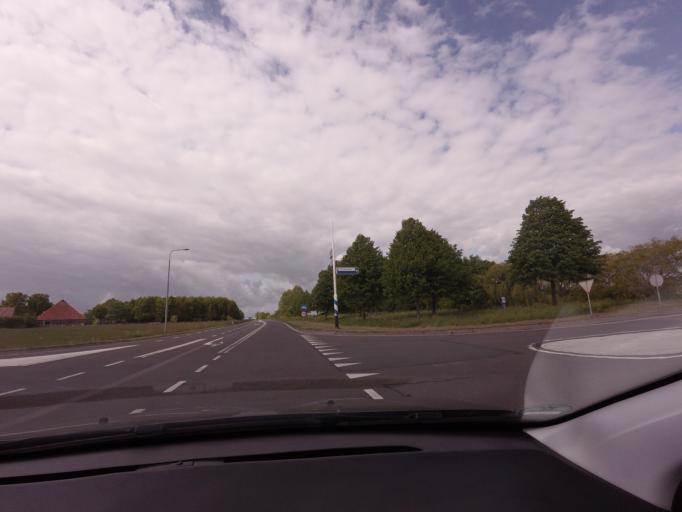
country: NL
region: Friesland
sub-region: Sudwest Fryslan
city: Koudum
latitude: 52.9208
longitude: 5.4616
